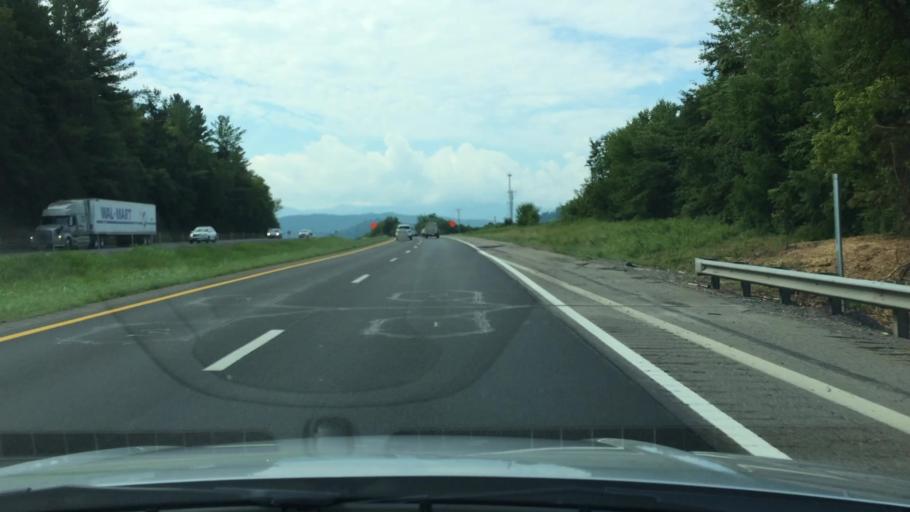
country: US
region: Tennessee
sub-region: Cocke County
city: Newport
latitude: 35.8893
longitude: -83.1871
